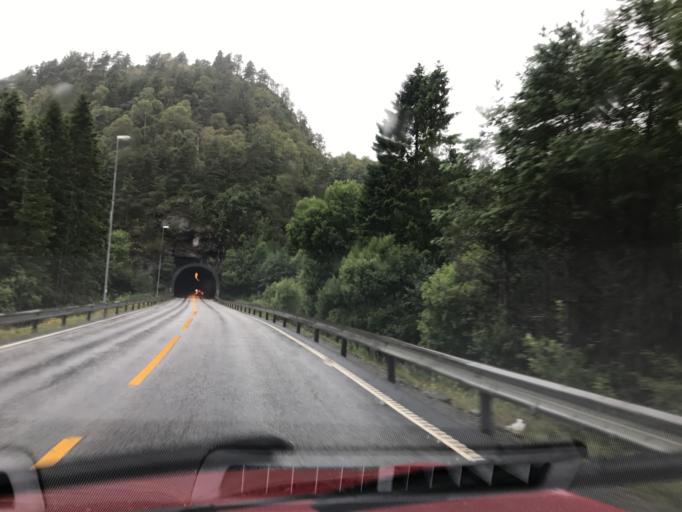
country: NO
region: Vest-Agder
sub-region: Flekkefjord
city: Flekkefjord
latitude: 58.2707
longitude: 6.7452
